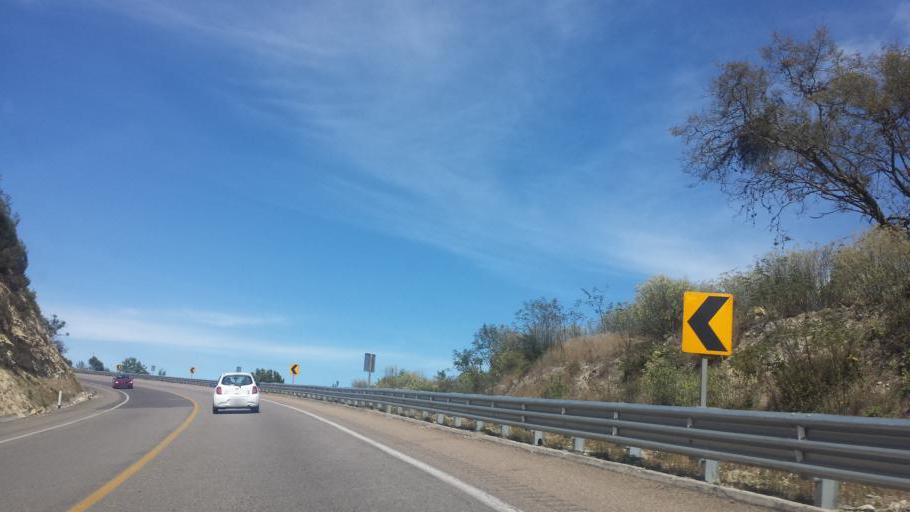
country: MX
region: Oaxaca
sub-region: Villa Tejupam de la Union
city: Villa Tejupam de la Union
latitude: 17.6551
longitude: -97.3394
